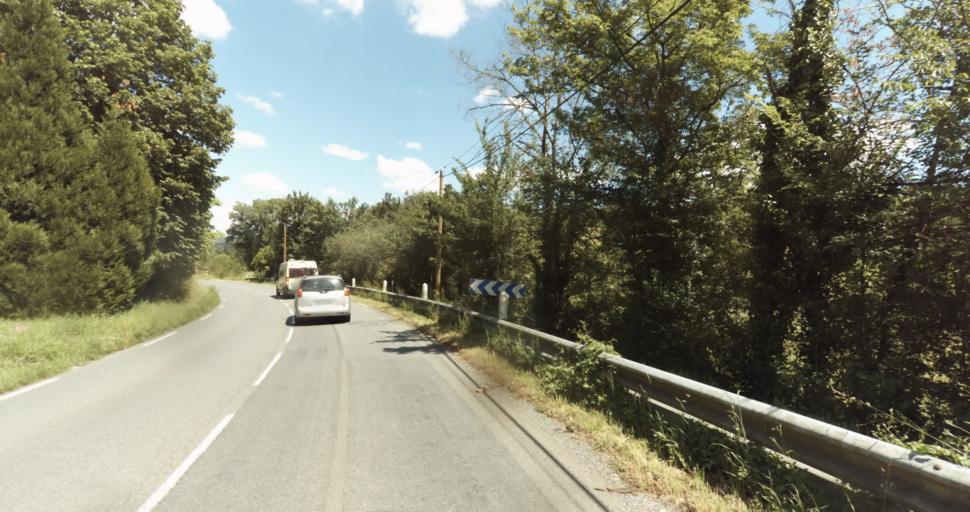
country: FR
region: Aquitaine
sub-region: Departement de la Dordogne
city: Le Bugue
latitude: 44.8430
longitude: 0.8912
